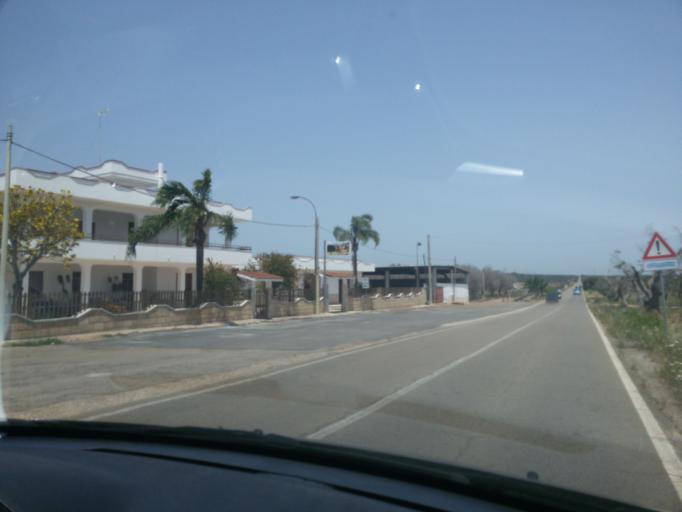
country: IT
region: Apulia
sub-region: Provincia di Lecce
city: Porto Cesareo
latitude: 40.2760
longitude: 17.9030
